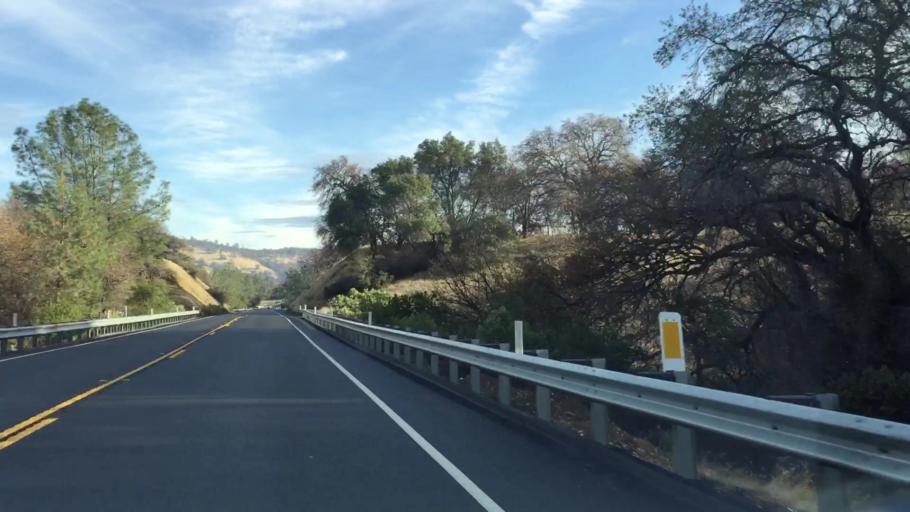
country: US
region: California
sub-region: Butte County
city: Paradise
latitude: 39.6418
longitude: -121.5714
